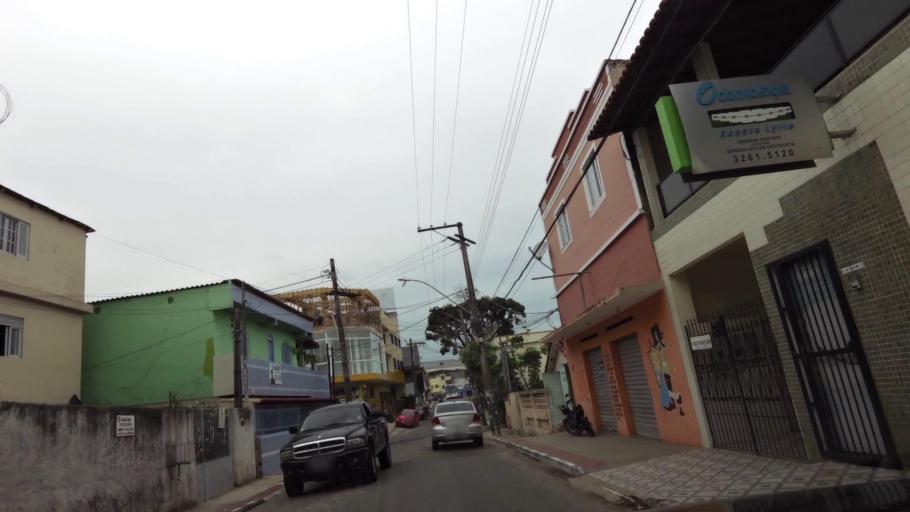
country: BR
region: Espirito Santo
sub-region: Guarapari
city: Guarapari
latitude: -20.6650
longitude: -40.5018
